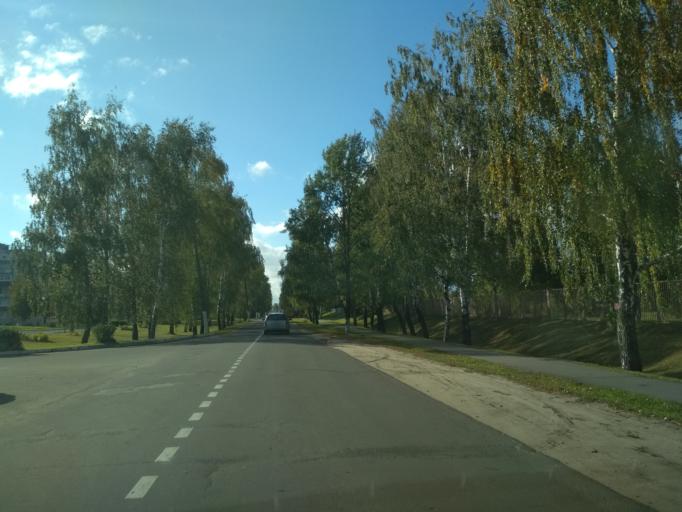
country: BY
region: Minsk
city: Mar''ina Horka
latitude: 53.5048
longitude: 28.1667
